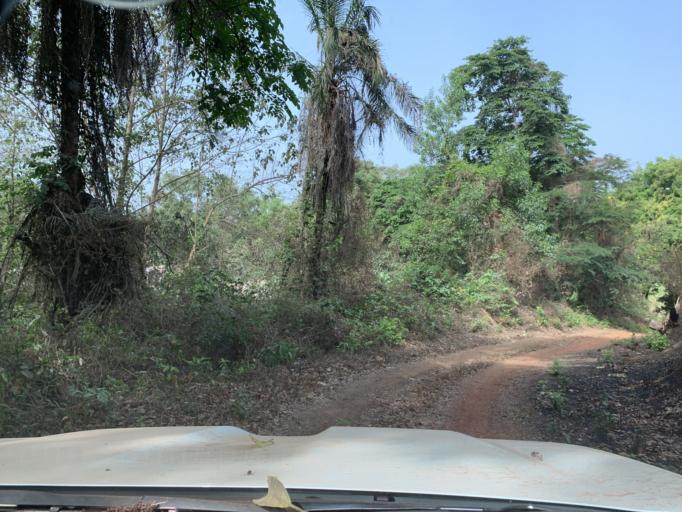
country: GN
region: Kindia
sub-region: Kindia
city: Kindia
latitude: 9.9749
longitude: -12.9829
